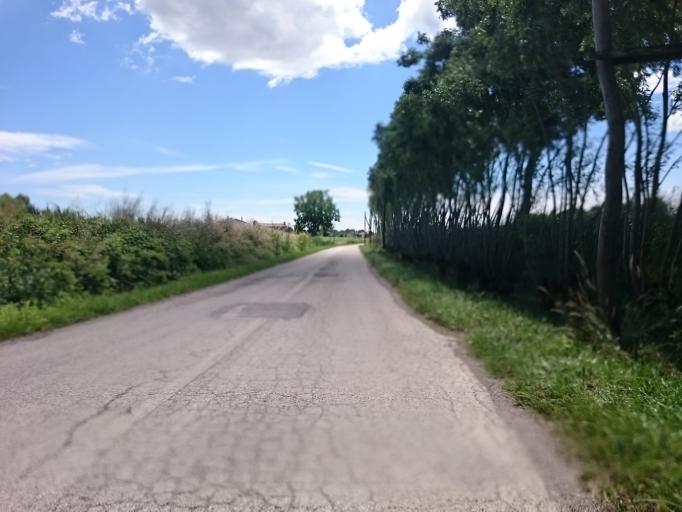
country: IT
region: Veneto
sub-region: Provincia di Padova
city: Brugine
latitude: 45.3071
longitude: 11.9822
